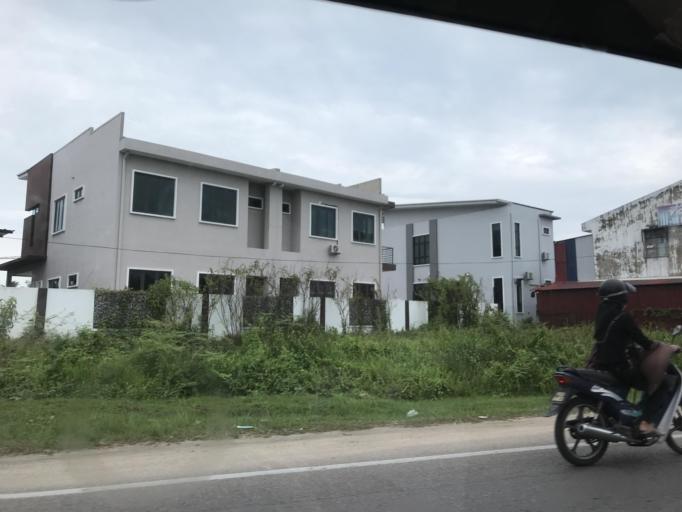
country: MY
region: Kelantan
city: Kota Bharu
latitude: 6.1301
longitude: 102.2130
